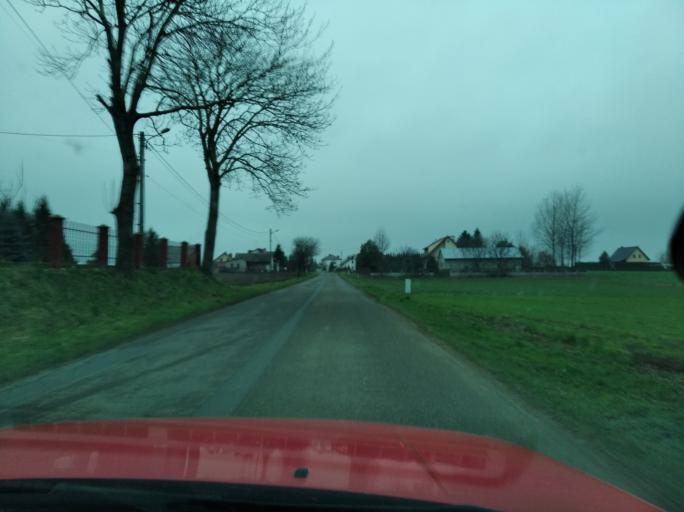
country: PL
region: Subcarpathian Voivodeship
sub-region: Powiat przeworski
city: Rozborz
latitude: 50.0636
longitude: 22.5315
